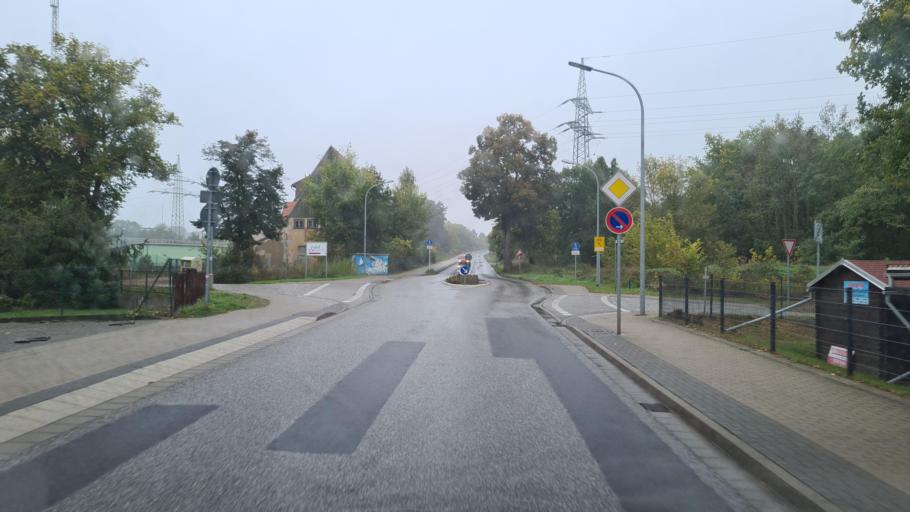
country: DE
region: Brandenburg
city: Furstenwalde
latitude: 52.3809
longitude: 14.0526
